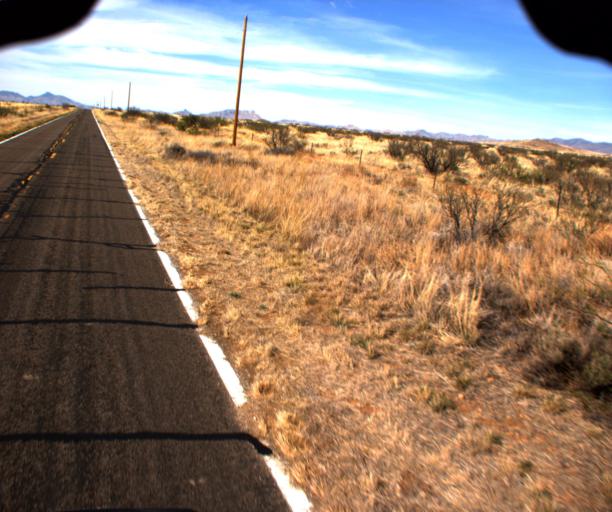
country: US
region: Arizona
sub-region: Cochise County
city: Willcox
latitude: 31.9196
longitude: -109.4914
